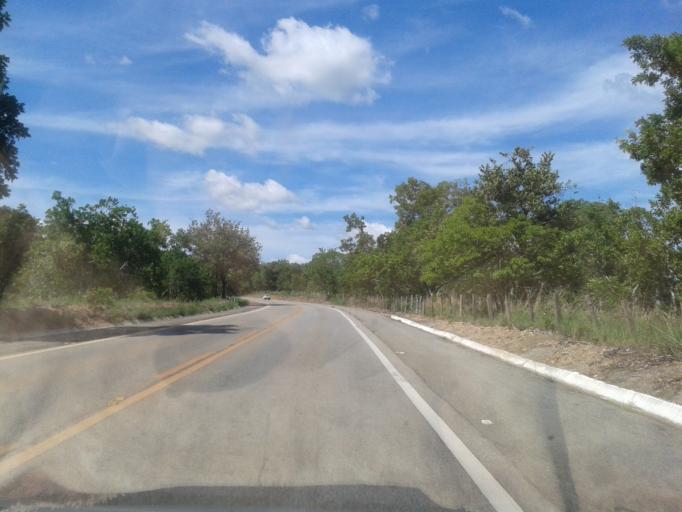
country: BR
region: Goias
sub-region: Itapuranga
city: Itapuranga
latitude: -15.3761
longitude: -50.3876
